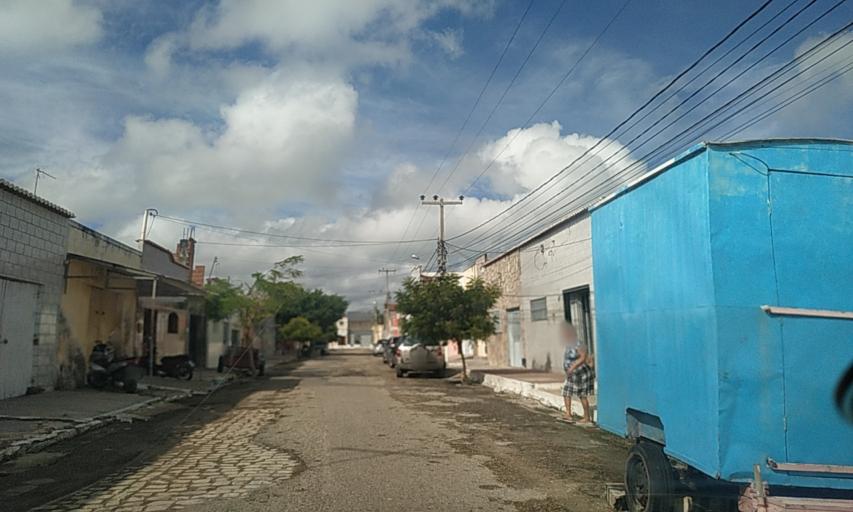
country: BR
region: Rio Grande do Norte
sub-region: Areia Branca
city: Areia Branca
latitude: -4.9578
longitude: -37.1332
